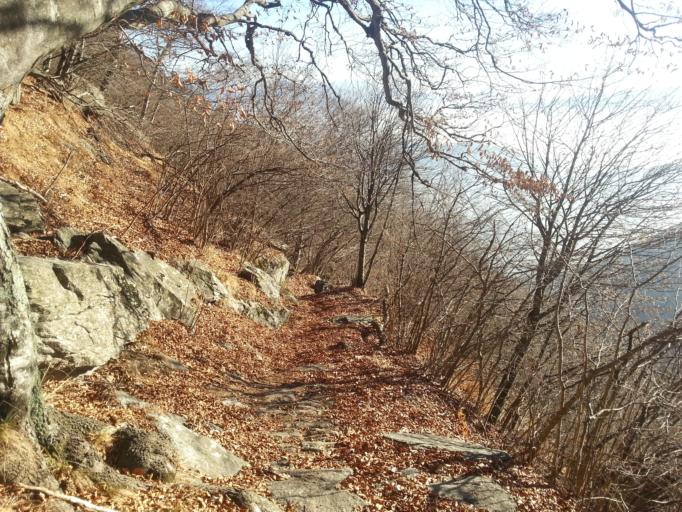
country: IT
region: Lombardy
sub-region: Provincia di Varese
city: Curiglia
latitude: 46.0432
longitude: 8.8436
